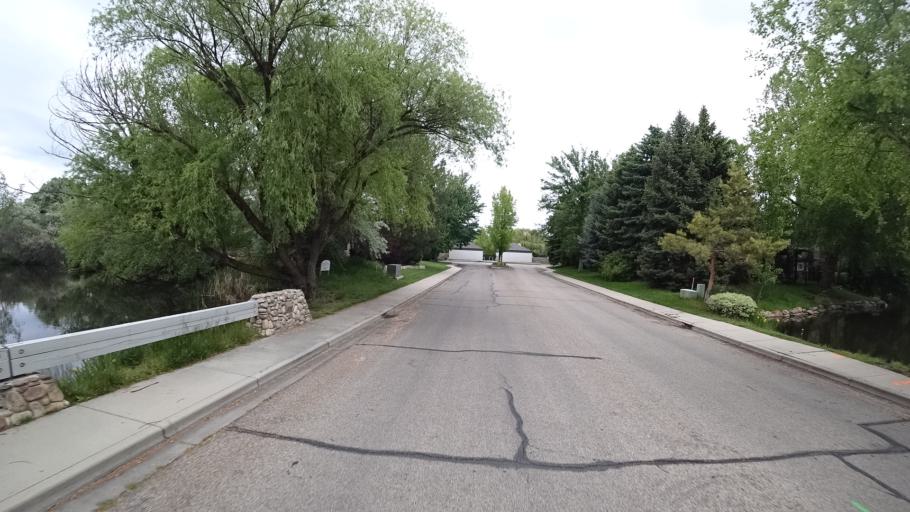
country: US
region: Idaho
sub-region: Ada County
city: Eagle
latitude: 43.6678
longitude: -116.2916
